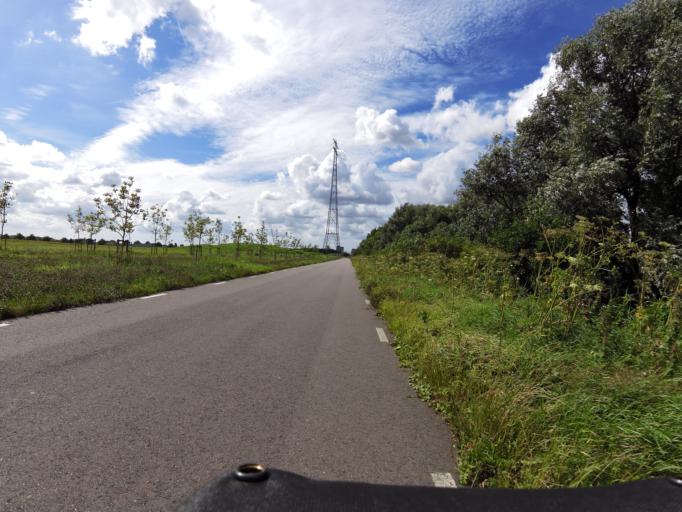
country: NL
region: South Holland
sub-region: Gemeente Oud-Beijerland
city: Oud-Beijerland
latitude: 51.8384
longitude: 4.3806
